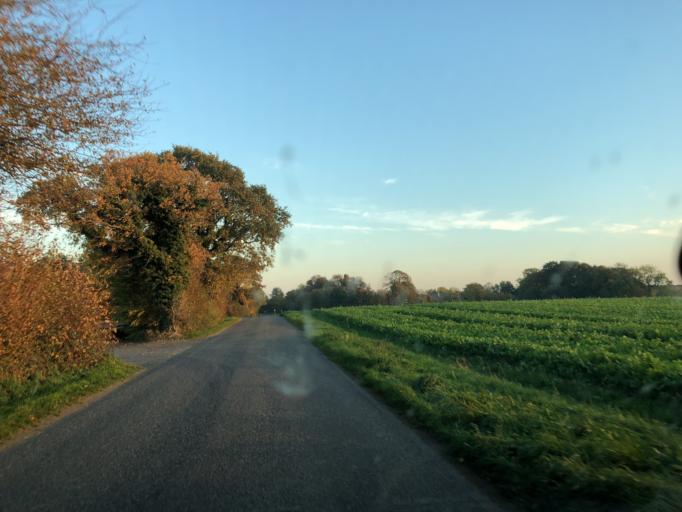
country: DK
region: South Denmark
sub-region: Vejle Kommune
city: Borkop
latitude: 55.6135
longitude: 9.6452
